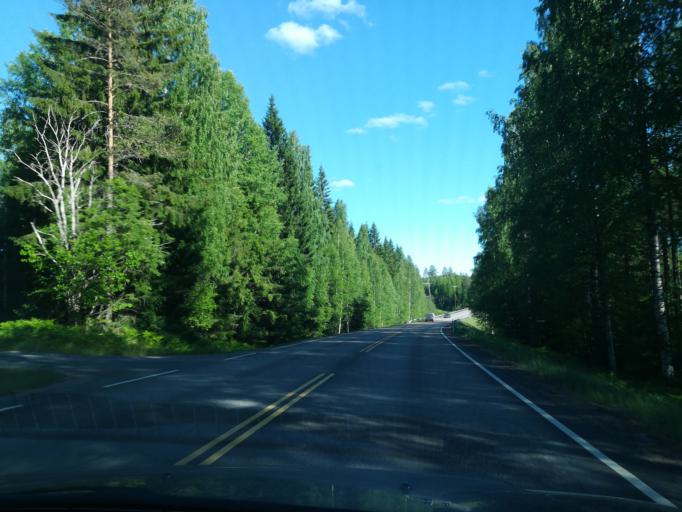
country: FI
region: South Karelia
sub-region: Imatra
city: Ruokolahti
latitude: 61.3885
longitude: 28.6493
